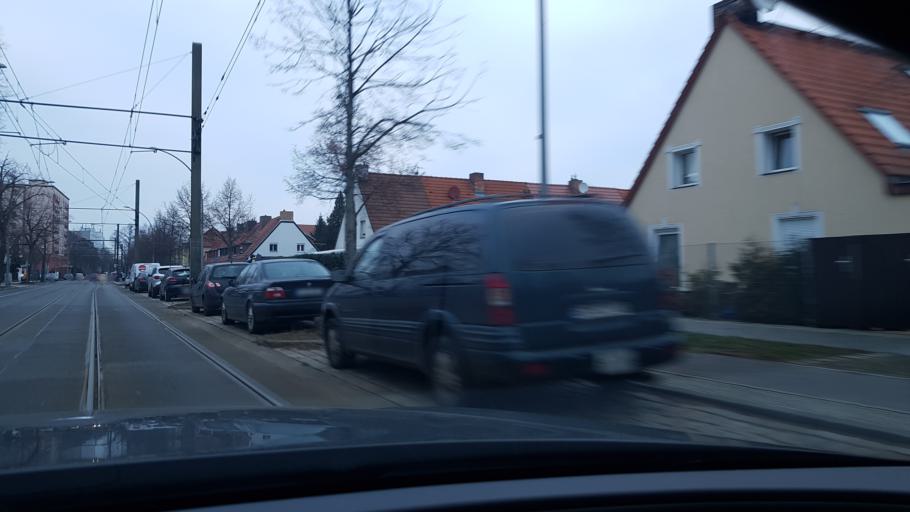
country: DE
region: Berlin
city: Berlin Koepenick
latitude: 52.4334
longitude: 13.5832
